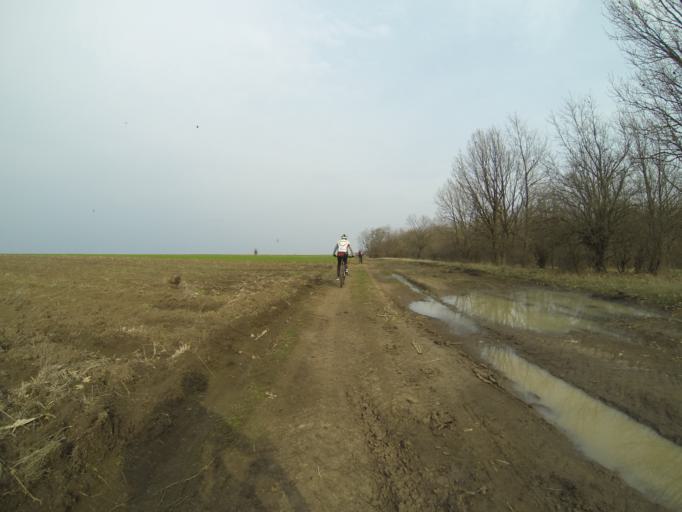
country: RO
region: Dolj
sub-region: Comuna Bucovat
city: Bucovat
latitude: 44.2593
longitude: 23.6900
